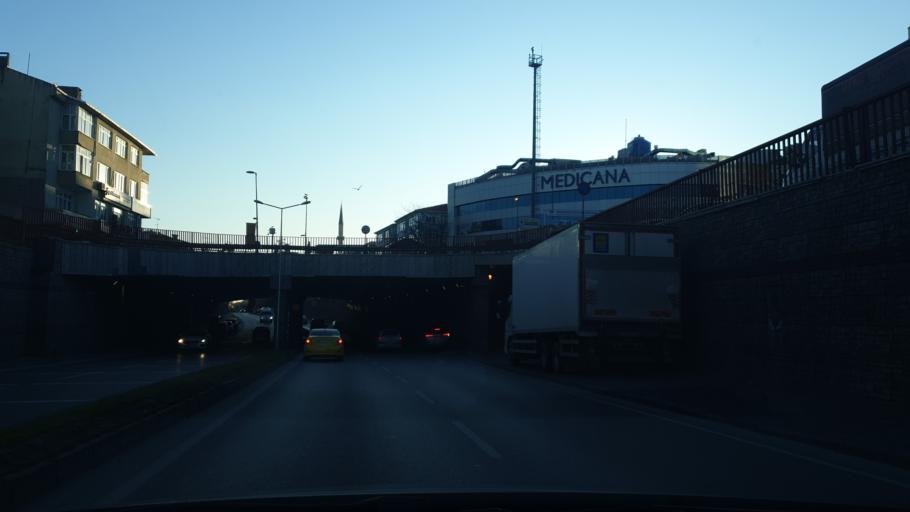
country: TR
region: Istanbul
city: Bahcelievler
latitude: 41.0066
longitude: 28.8714
